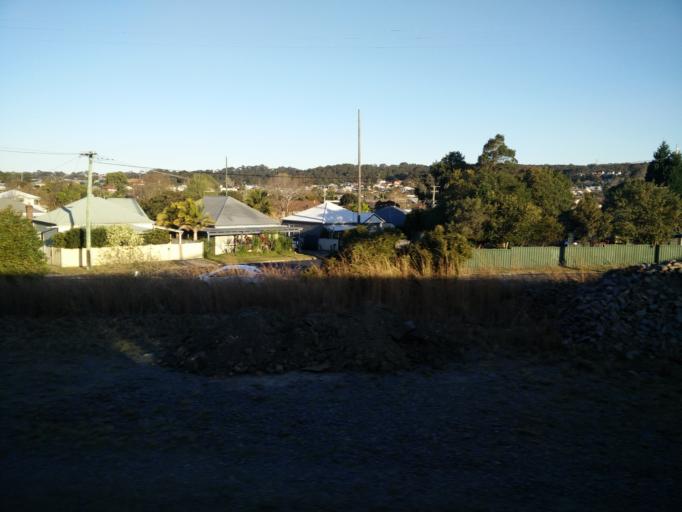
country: AU
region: New South Wales
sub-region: Newcastle
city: Broadmeadow
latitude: -32.9347
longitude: 151.7188
